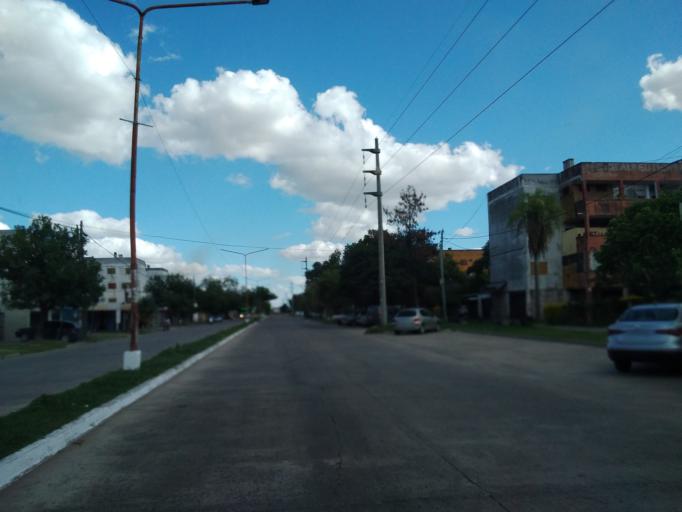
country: AR
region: Corrientes
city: Corrientes
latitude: -27.4956
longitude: -58.8268
